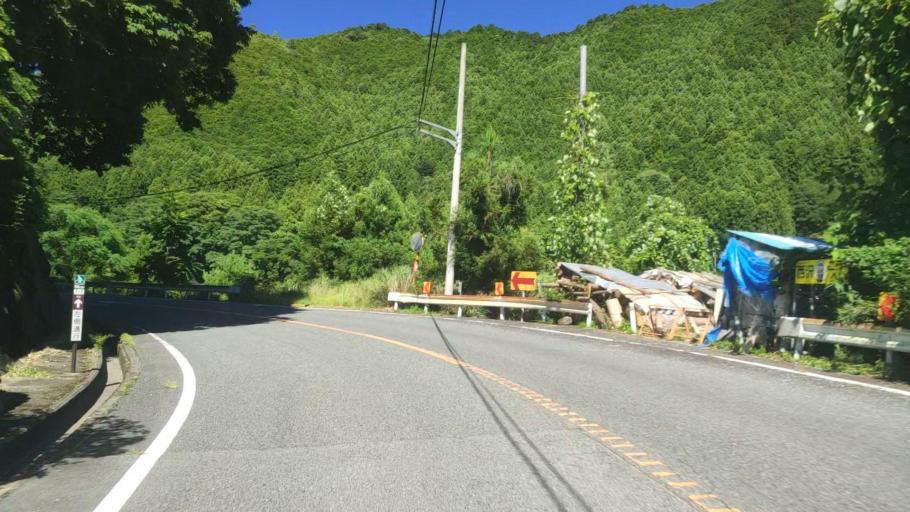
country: JP
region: Nara
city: Yoshino-cho
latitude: 34.3767
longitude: 135.9166
